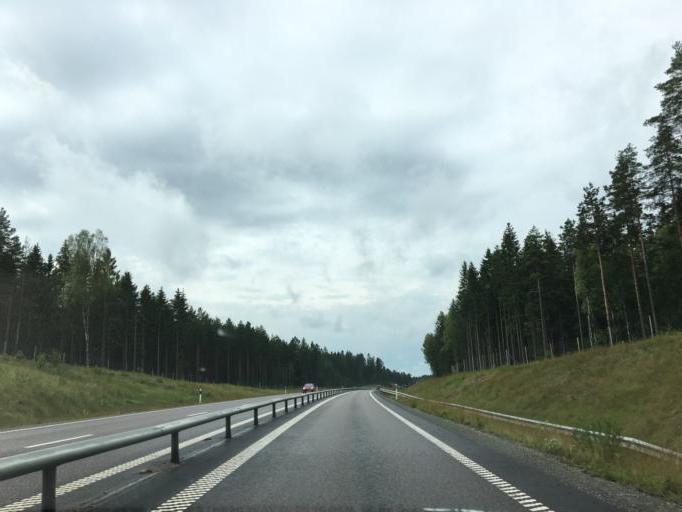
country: SE
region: Soedermanland
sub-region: Katrineholms Kommun
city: Katrineholm
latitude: 58.9784
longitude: 16.2658
